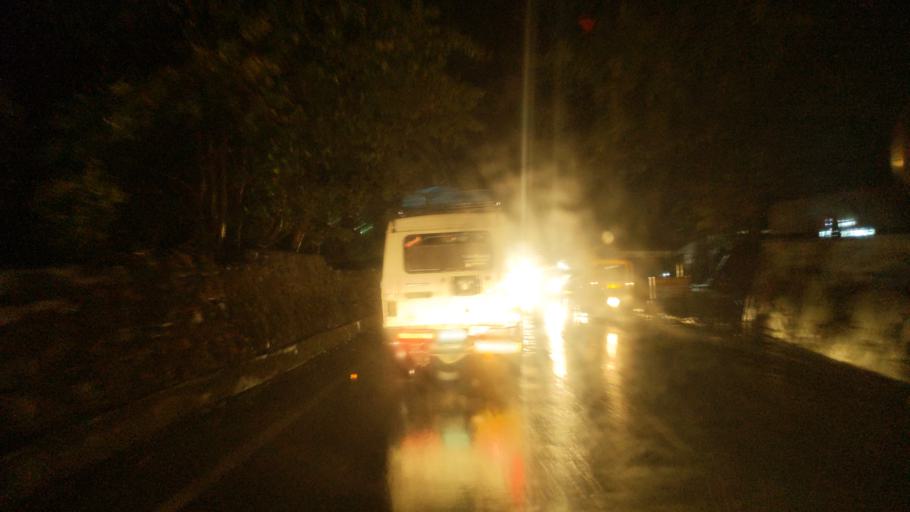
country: IN
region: Uttarakhand
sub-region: Naini Tal
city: Haldwani
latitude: 29.2669
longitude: 79.5447
